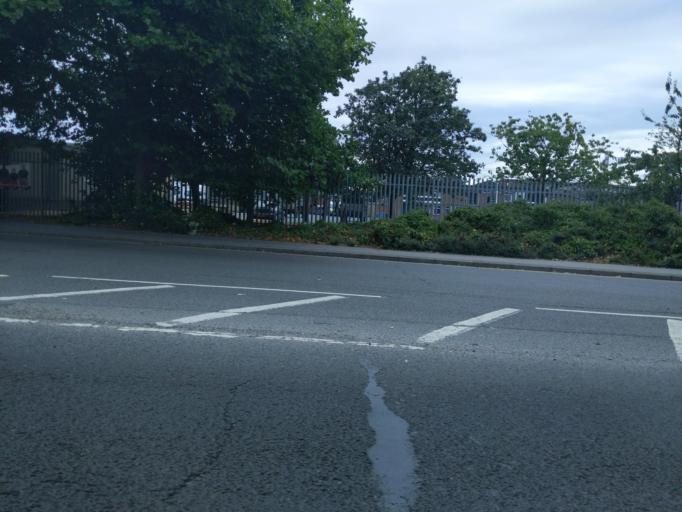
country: GB
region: England
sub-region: Greater London
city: Croydon
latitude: 51.3781
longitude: -0.1091
